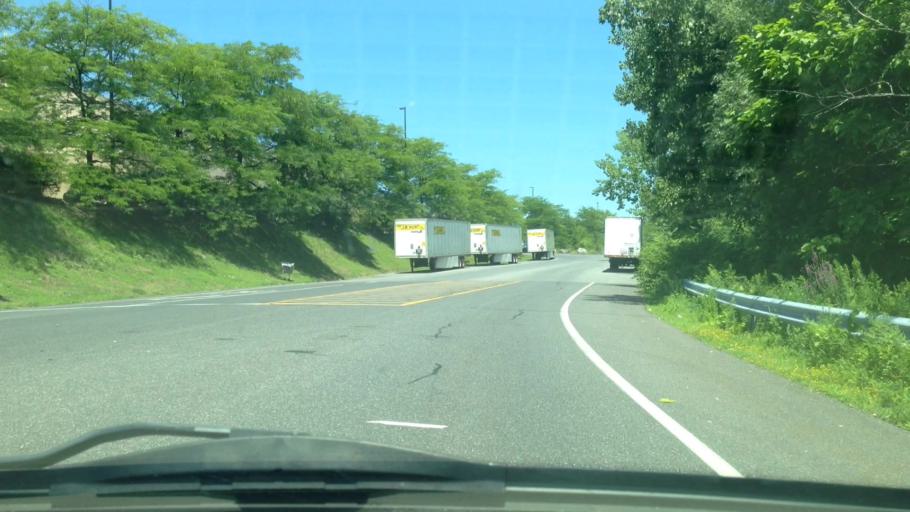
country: US
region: New York
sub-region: Ulster County
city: Lake Katrine
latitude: 41.9697
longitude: -73.9825
